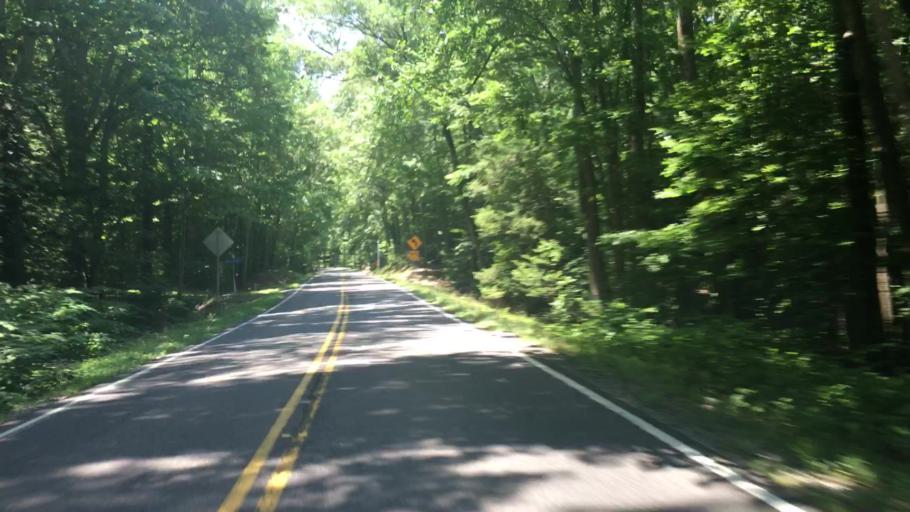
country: US
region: Virginia
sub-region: King George County
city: Dahlgren
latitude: 38.3355
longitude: -77.1323
